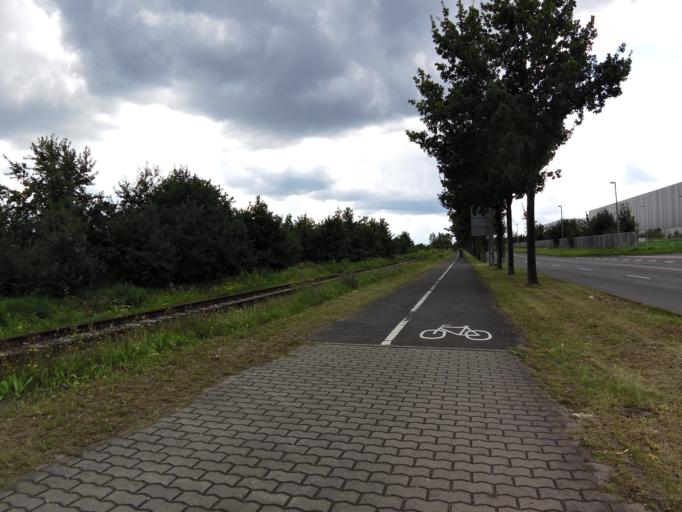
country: DE
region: Saxony
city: Rackwitz
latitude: 51.3930
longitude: 12.4124
